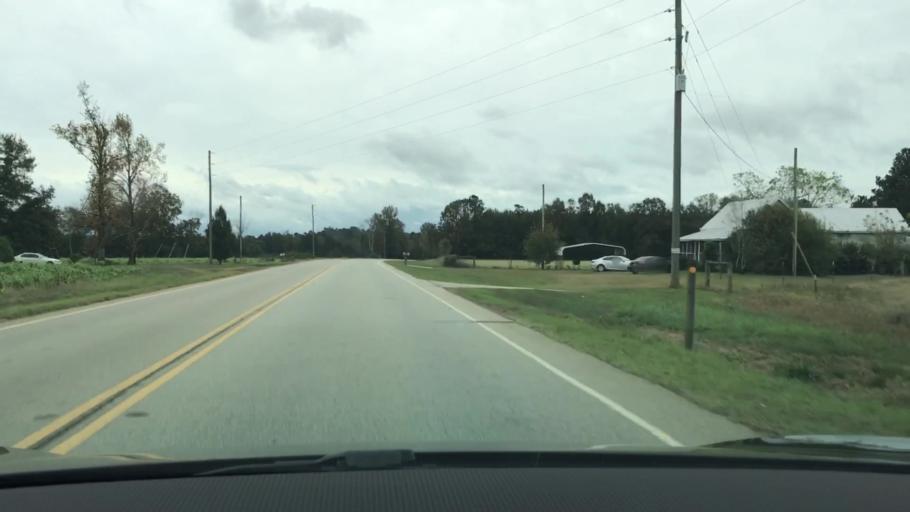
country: US
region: Georgia
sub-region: Jefferson County
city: Louisville
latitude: 33.0993
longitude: -82.4212
